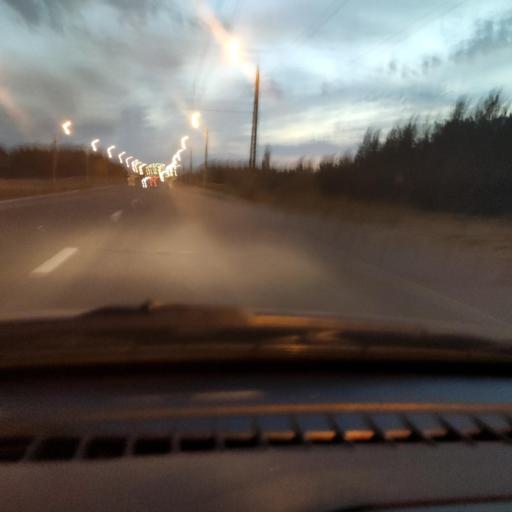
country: RU
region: Samara
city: Zhigulevsk
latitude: 53.5245
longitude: 49.5450
